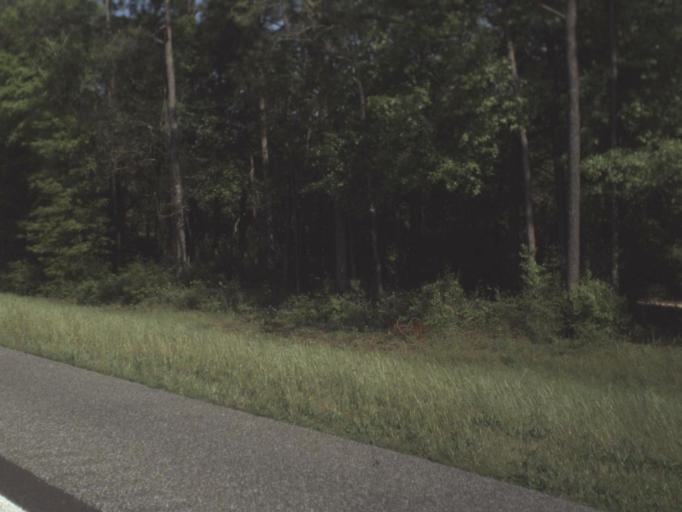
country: US
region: Florida
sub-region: Santa Rosa County
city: East Milton
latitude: 30.6500
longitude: -86.8902
